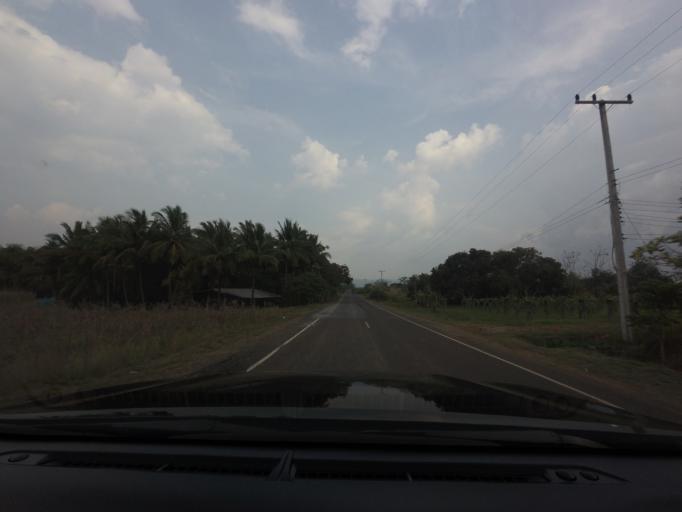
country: TH
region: Nakhon Ratchasima
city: Wang Nam Khiao
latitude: 14.4167
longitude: 101.7823
